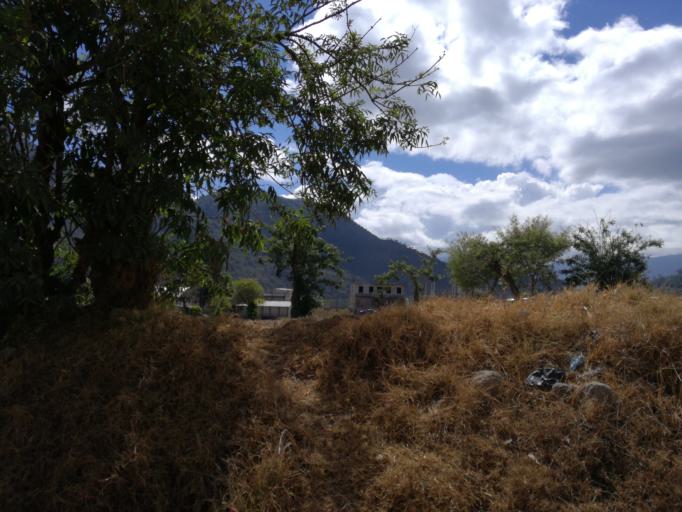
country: GT
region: Quetzaltenango
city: Almolonga
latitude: 14.7888
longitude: -91.5443
